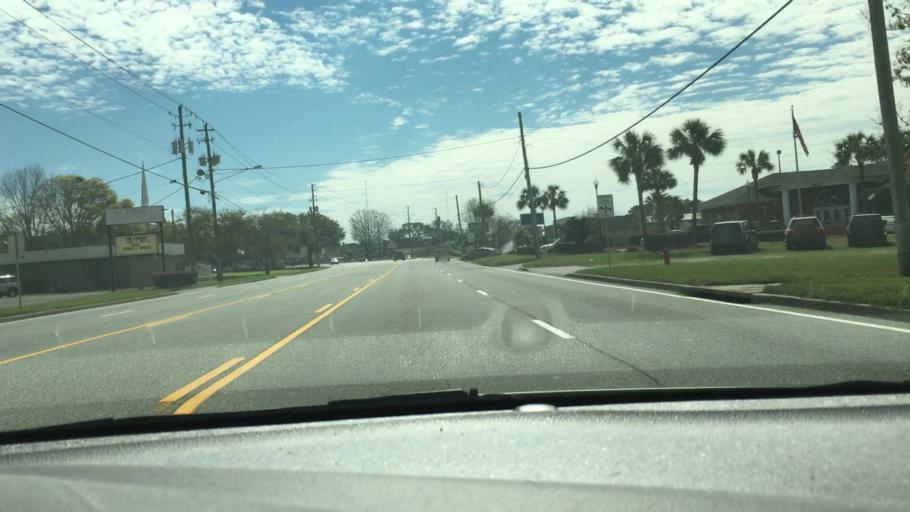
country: US
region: Georgia
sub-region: Glynn County
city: Dock Junction
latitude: 31.1979
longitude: -81.4907
